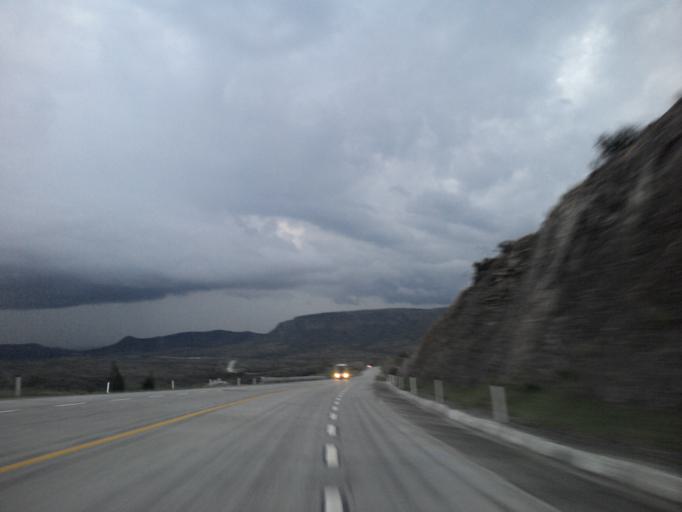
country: MX
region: Zacatecas
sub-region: Cuauhtemoc
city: Piedra Gorda
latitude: 22.5722
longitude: -102.3924
